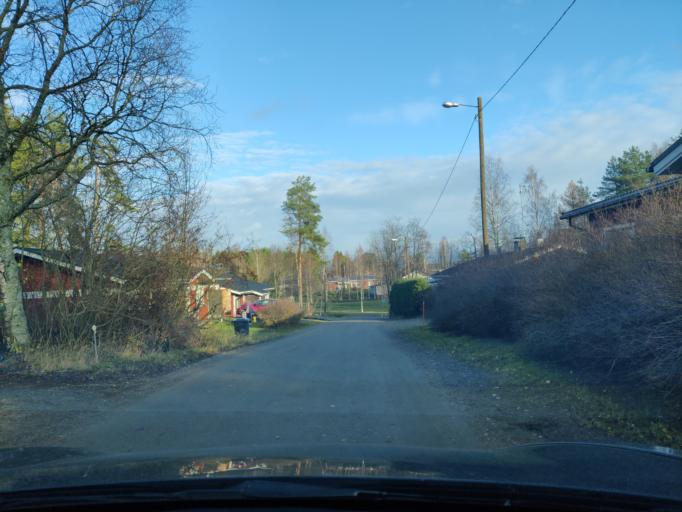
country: FI
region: Northern Savo
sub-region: Ylae-Savo
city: Kiuruvesi
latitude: 63.6466
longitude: 26.6282
